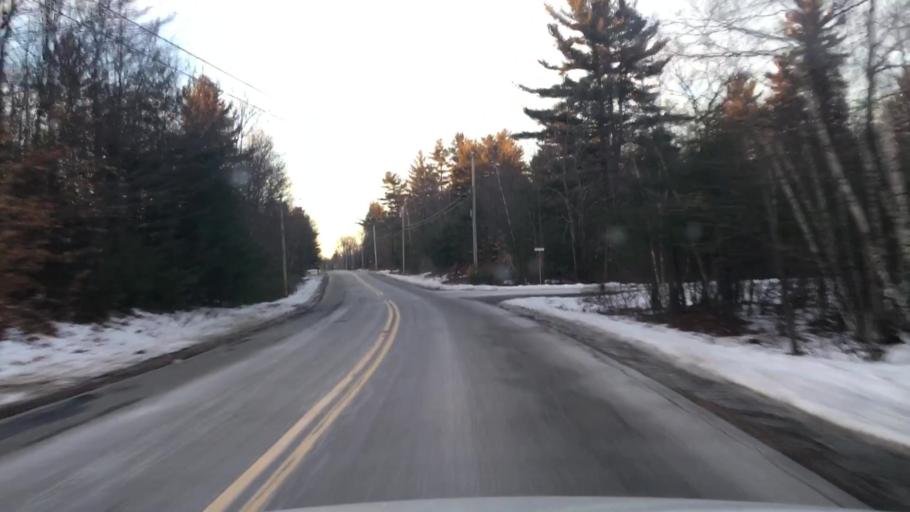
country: US
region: Maine
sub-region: York County
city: Lebanon
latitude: 43.3471
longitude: -70.8659
